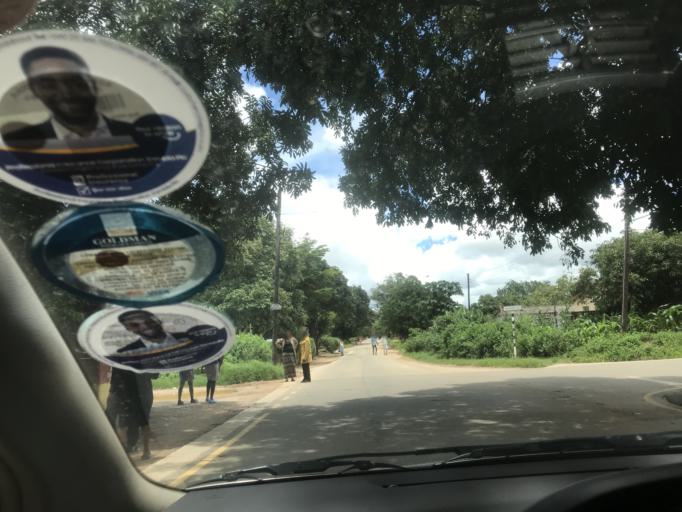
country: ZM
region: Lusaka
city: Lusaka
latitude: -15.4246
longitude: 28.3037
